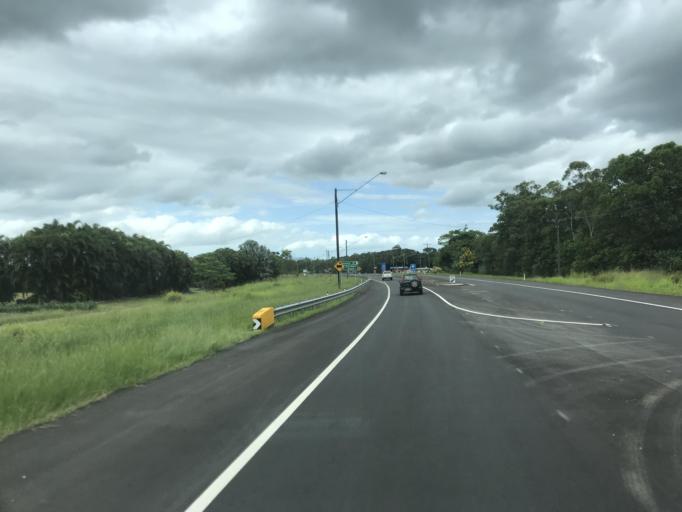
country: AU
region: Queensland
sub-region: Cassowary Coast
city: Innisfail
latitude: -17.7454
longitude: 146.0287
